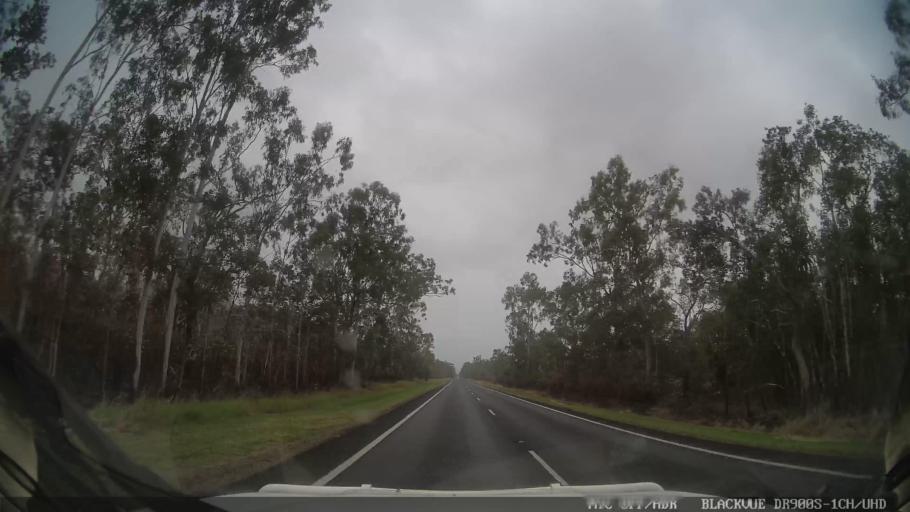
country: AU
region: Queensland
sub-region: Hinchinbrook
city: Ingham
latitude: -18.4334
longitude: 146.1392
